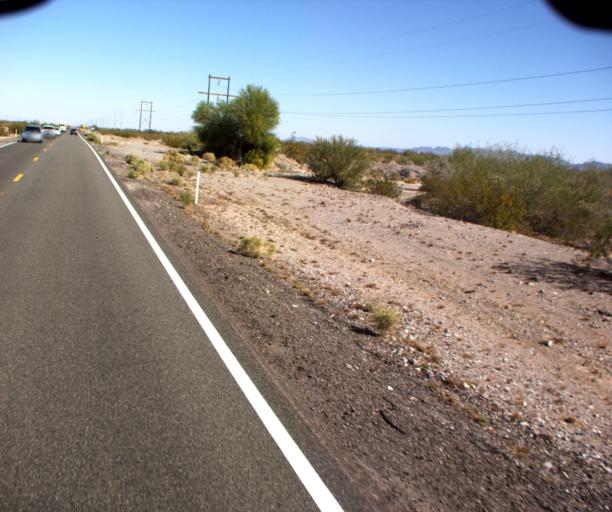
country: US
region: Arizona
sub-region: La Paz County
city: Quartzsite
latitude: 33.5710
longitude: -114.2170
